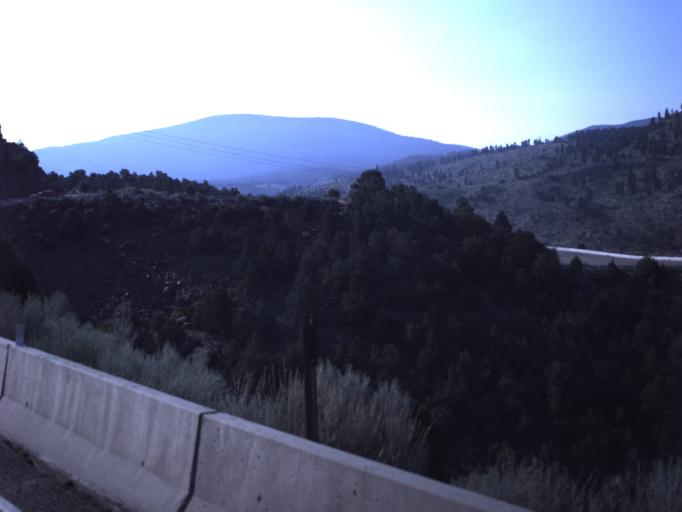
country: US
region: Utah
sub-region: Daggett County
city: Manila
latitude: 40.9130
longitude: -109.4191
